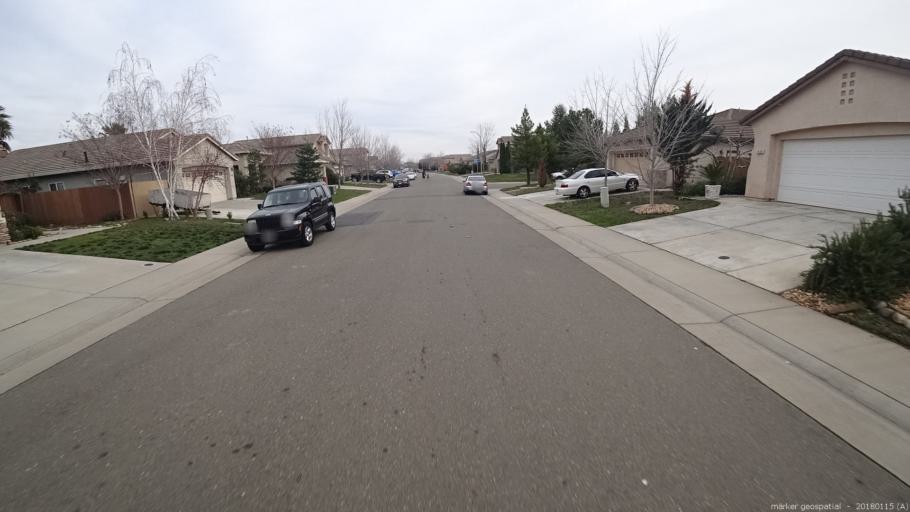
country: US
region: California
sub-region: Sacramento County
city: Rancho Cordova
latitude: 38.5738
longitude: -121.2775
